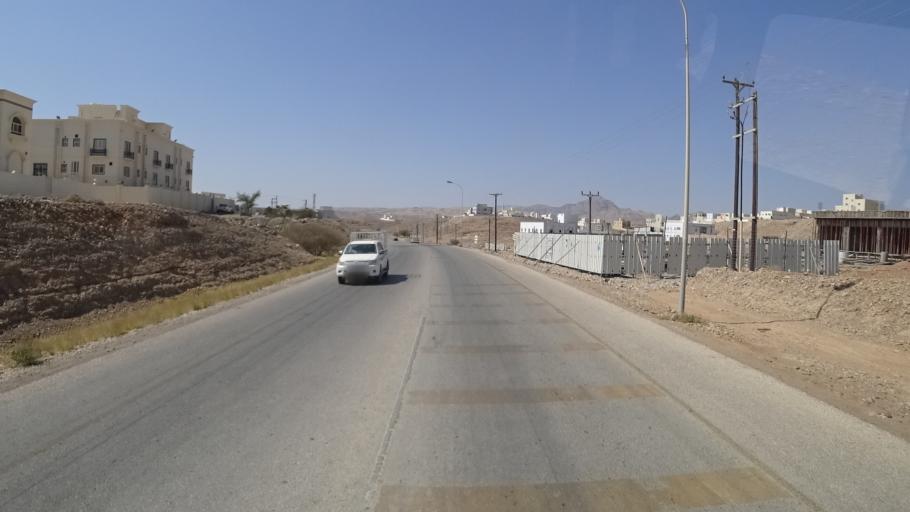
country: OM
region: Ash Sharqiyah
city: Sur
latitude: 22.5556
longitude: 59.4987
